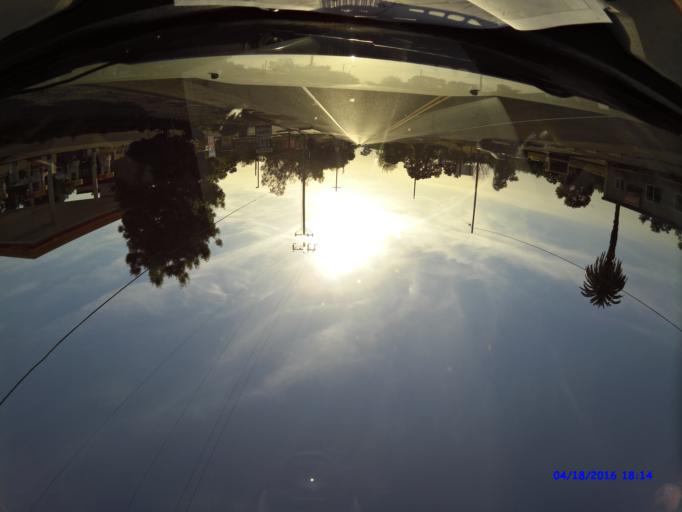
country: US
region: California
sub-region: San Joaquin County
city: Linden
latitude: 37.9302
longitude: -121.0008
